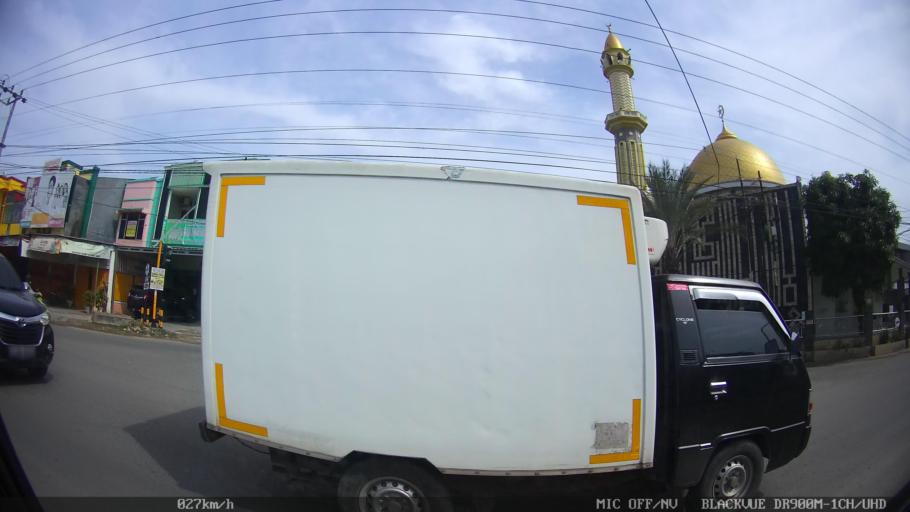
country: ID
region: Lampung
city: Kedaton
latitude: -5.3869
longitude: 105.2919
